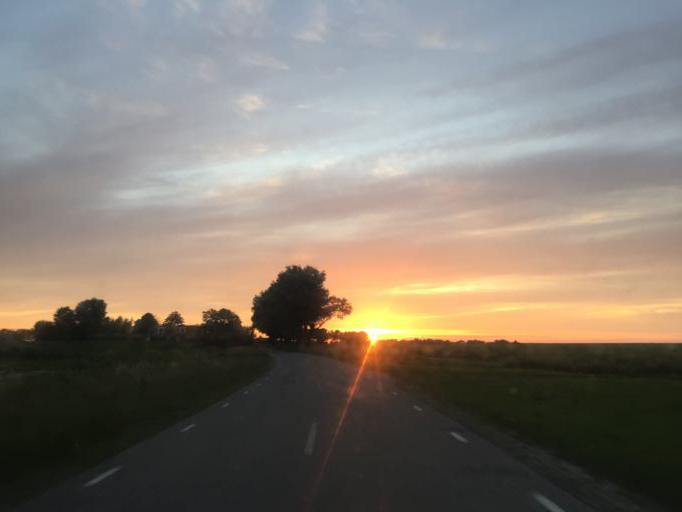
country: NL
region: Friesland
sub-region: Gemeente Dongeradeel
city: Anjum
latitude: 53.3882
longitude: 6.1086
